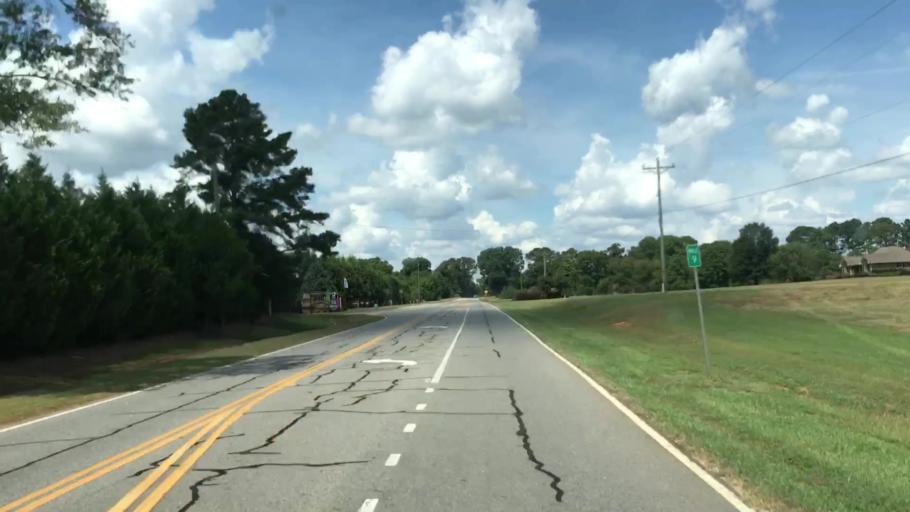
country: US
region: Georgia
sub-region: Oconee County
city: Watkinsville
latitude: 33.8336
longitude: -83.3800
